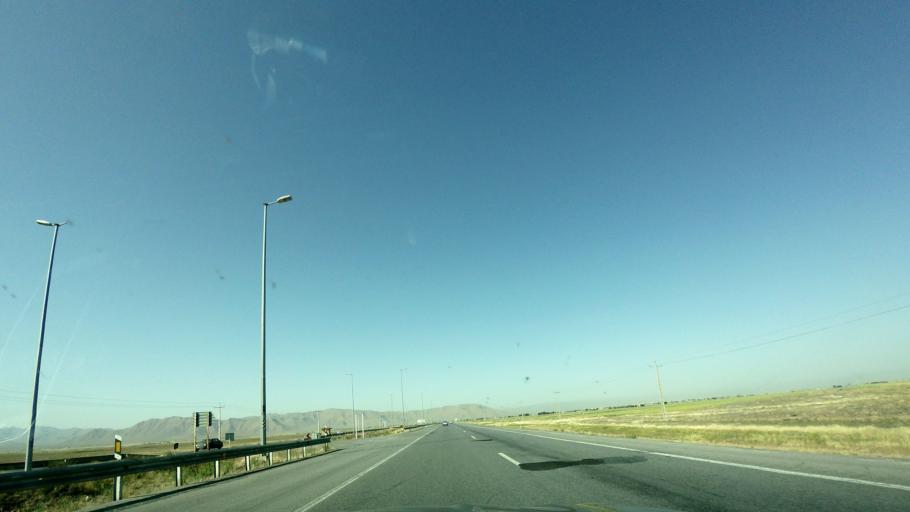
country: IR
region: Markazi
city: Ashtian
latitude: 34.1820
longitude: 50.0465
